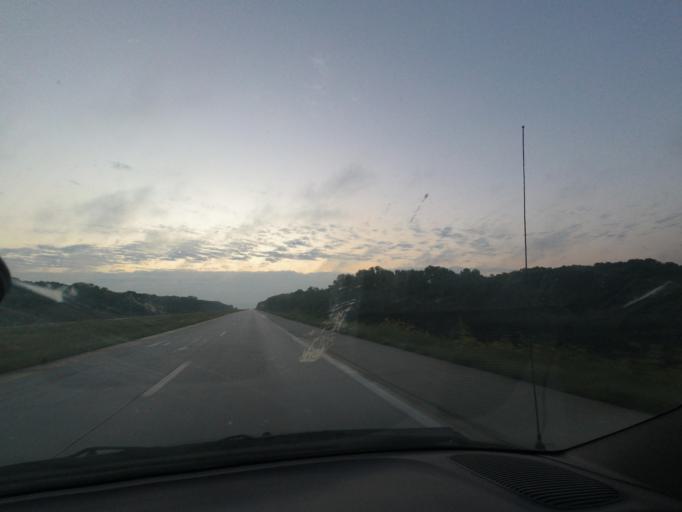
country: US
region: Missouri
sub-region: Linn County
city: Marceline
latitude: 39.7590
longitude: -92.8439
